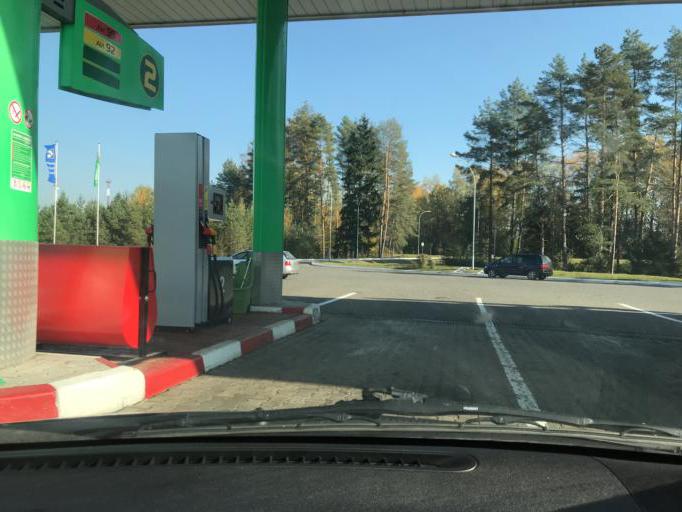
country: BY
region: Minsk
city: Uzda
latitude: 53.4268
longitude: 27.4951
